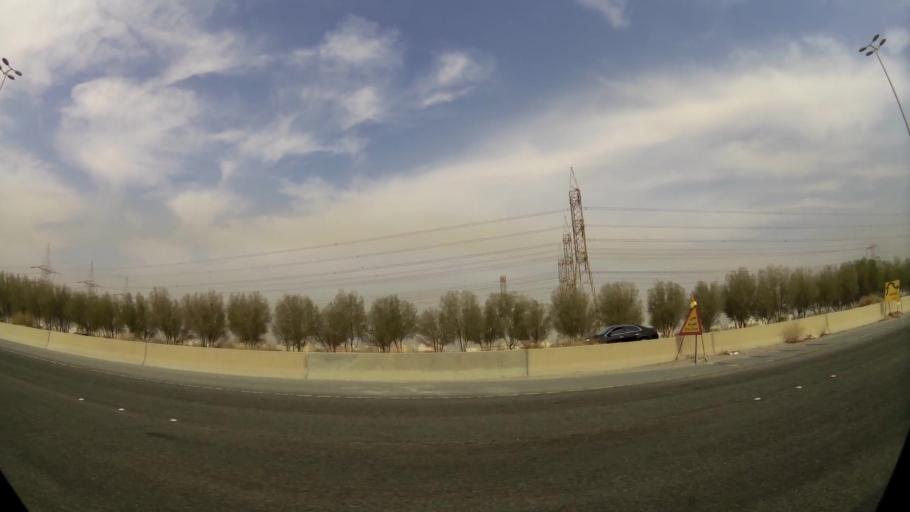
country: KW
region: Muhafazat al Jahra'
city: Al Jahra'
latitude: 29.3299
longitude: 47.7894
